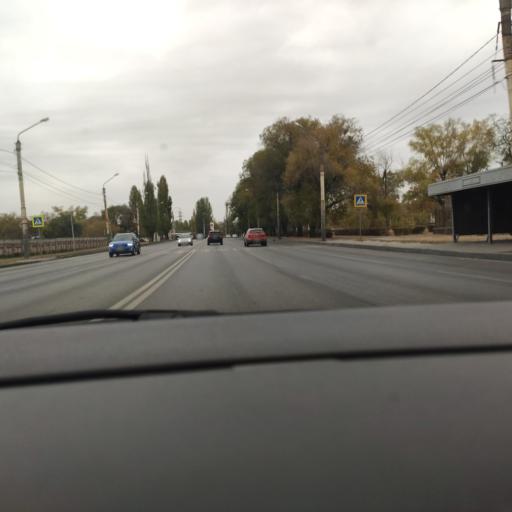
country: RU
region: Voronezj
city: Voronezh
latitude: 51.6267
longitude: 39.2313
